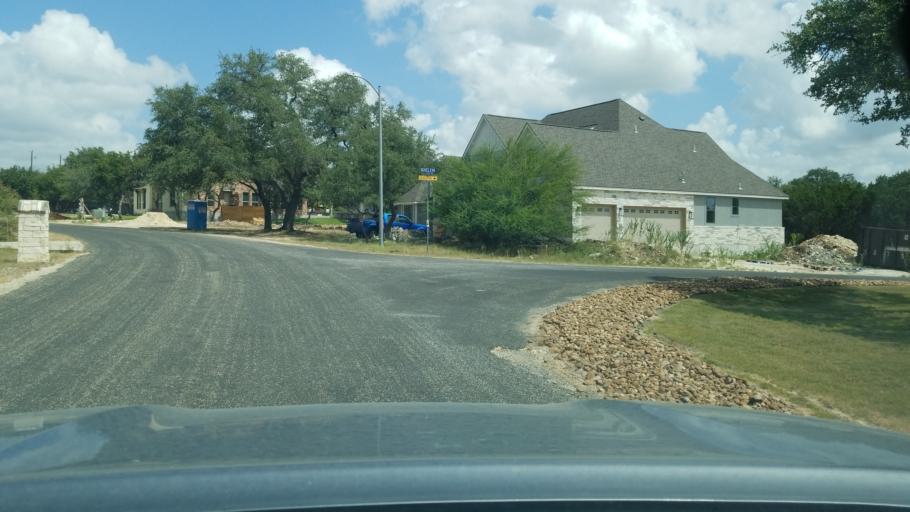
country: US
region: Texas
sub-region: Bexar County
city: Timberwood Park
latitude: 29.6977
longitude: -98.4973
